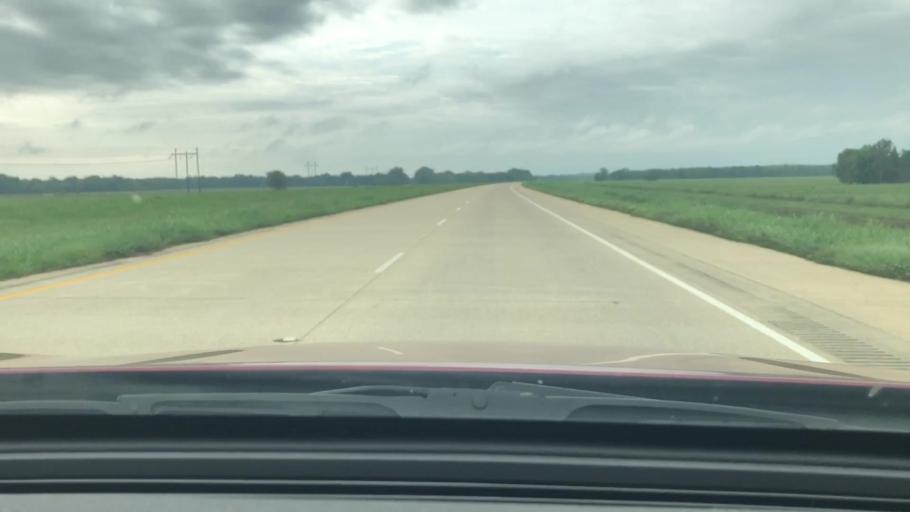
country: US
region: Louisiana
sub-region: Caddo Parish
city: Blanchard
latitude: 32.6591
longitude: -93.8438
